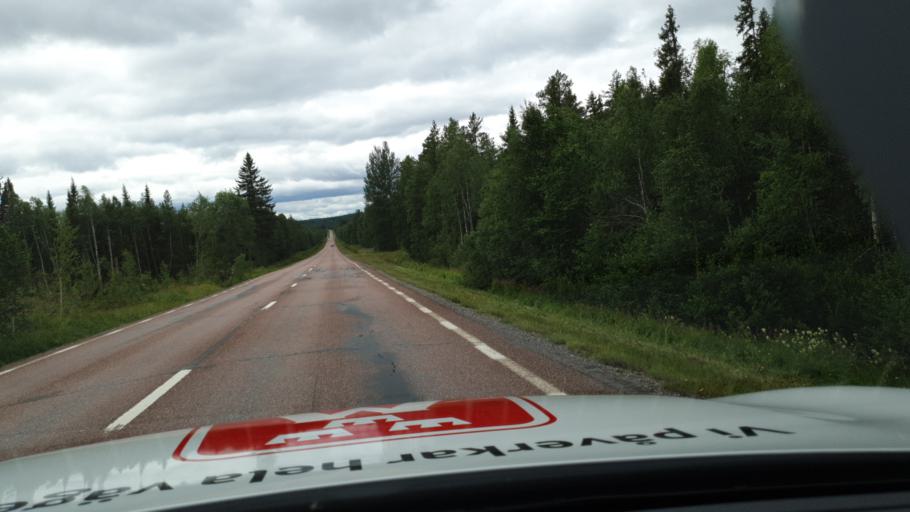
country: SE
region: Jaemtland
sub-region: Stroemsunds Kommun
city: Stroemsund
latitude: 63.9052
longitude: 15.7275
